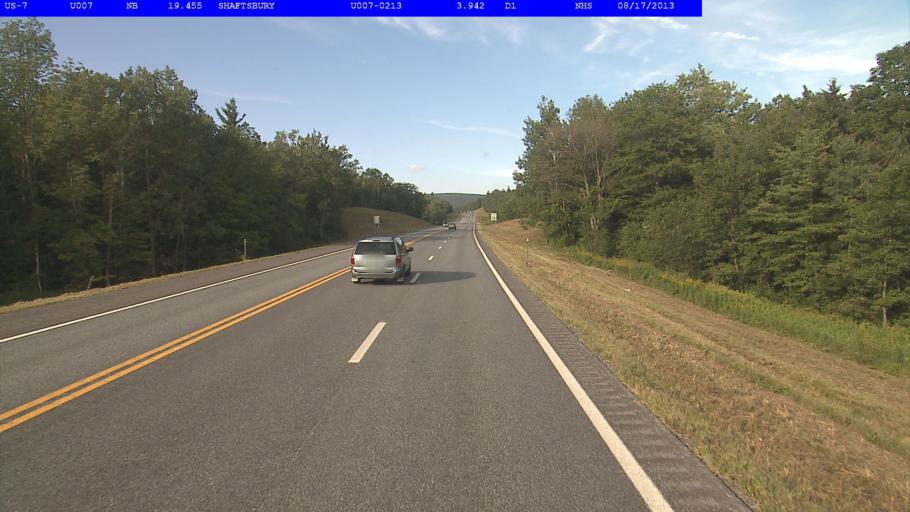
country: US
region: Vermont
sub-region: Bennington County
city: Arlington
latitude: 42.9826
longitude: -73.1525
